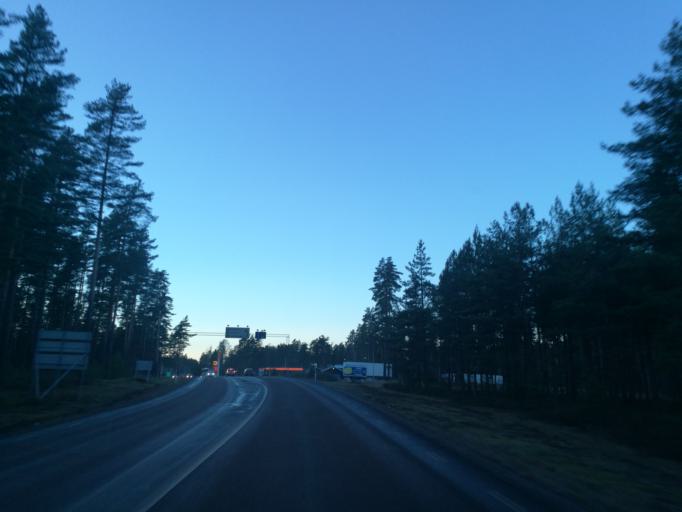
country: SE
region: Vaermland
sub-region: Eda Kommun
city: Charlottenberg
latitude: 59.9295
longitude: 12.2464
